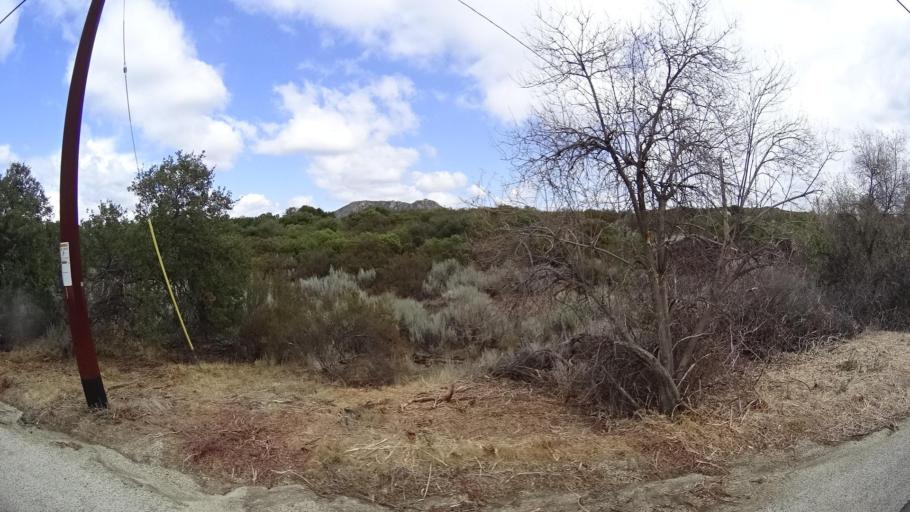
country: US
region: California
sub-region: San Diego County
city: Campo
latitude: 32.6706
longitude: -116.5023
